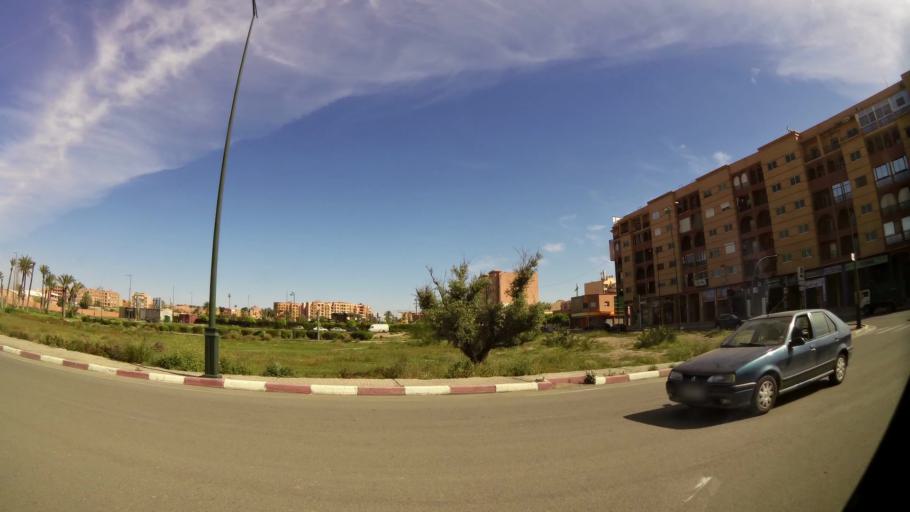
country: MA
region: Marrakech-Tensift-Al Haouz
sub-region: Marrakech
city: Marrakesh
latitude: 31.6576
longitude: -8.0223
